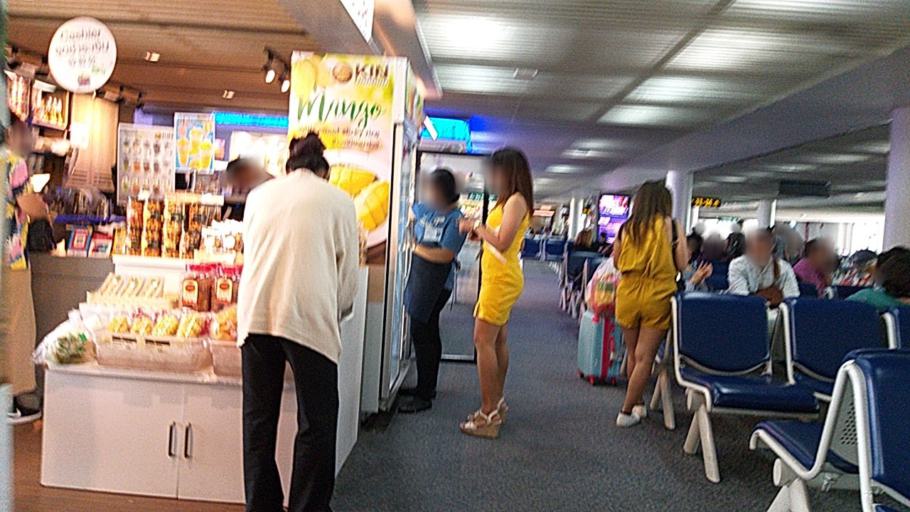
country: TH
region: Bangkok
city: Don Mueang
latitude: 13.9211
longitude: 100.6038
